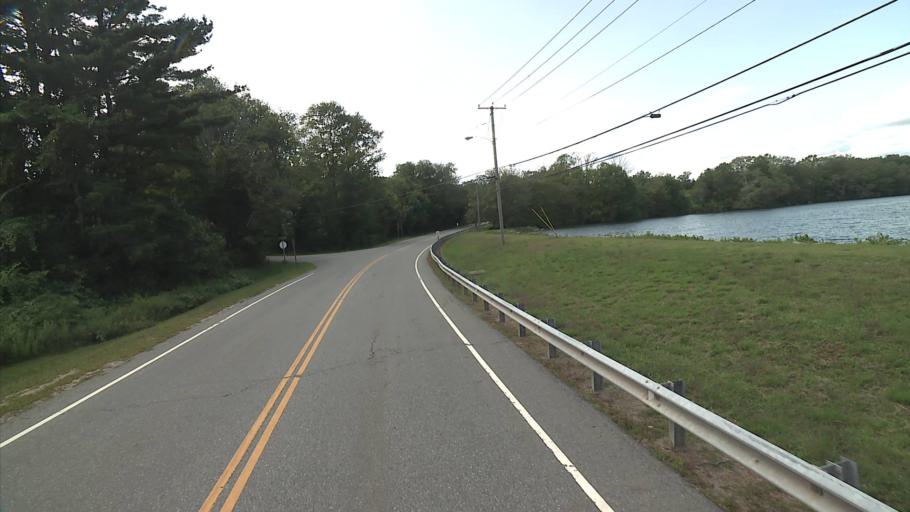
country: US
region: Connecticut
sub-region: New London County
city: Colchester
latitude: 41.6293
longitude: -72.3017
